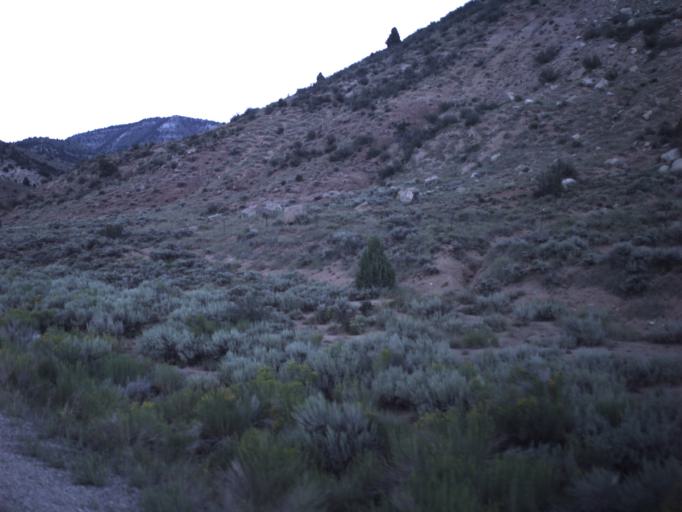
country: US
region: Utah
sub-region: Carbon County
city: Helper
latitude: 39.8277
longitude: -110.7882
